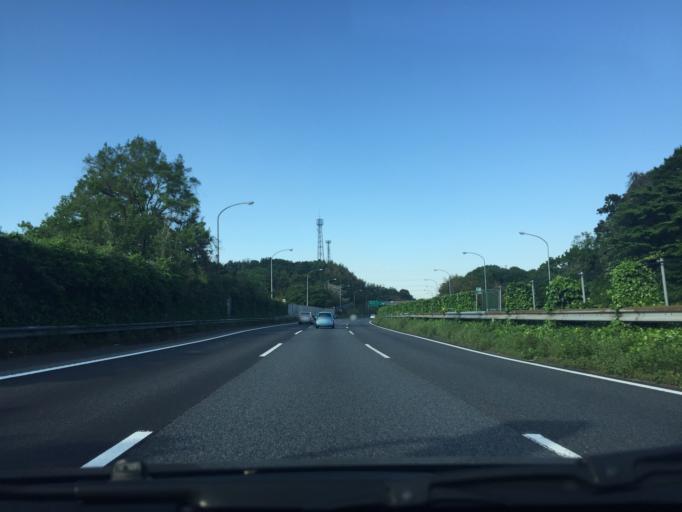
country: JP
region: Tokyo
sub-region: Machida-shi
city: Machida
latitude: 35.5126
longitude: 139.4882
